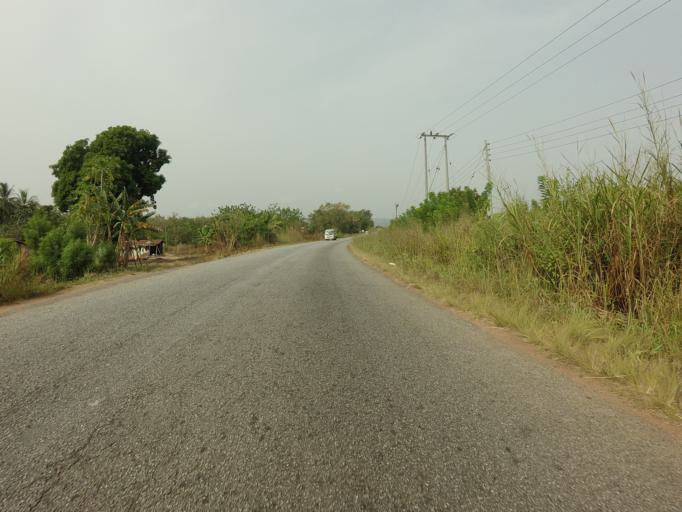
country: GH
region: Volta
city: Ho
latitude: 6.5727
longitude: 0.3636
